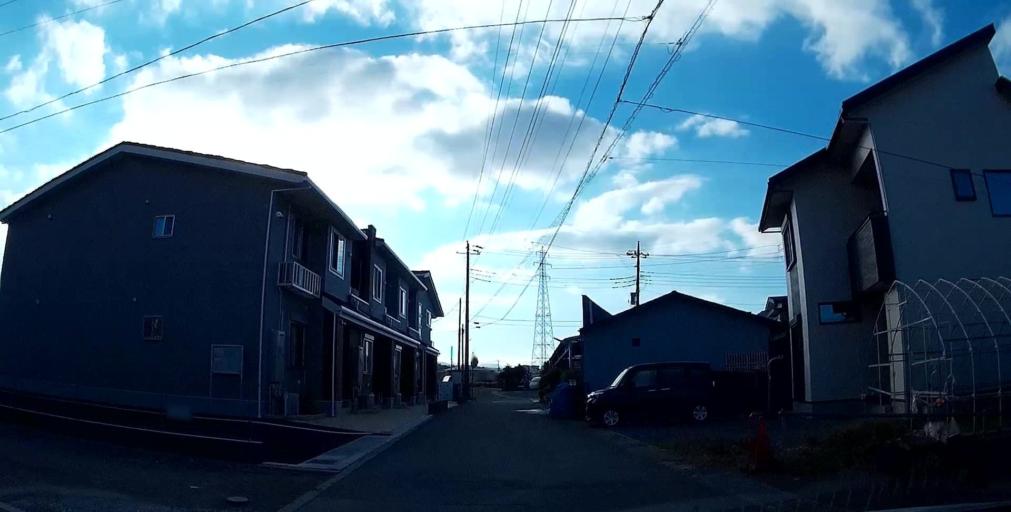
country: JP
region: Yamanashi
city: Fujikawaguchiko
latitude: 35.4940
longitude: 138.8196
